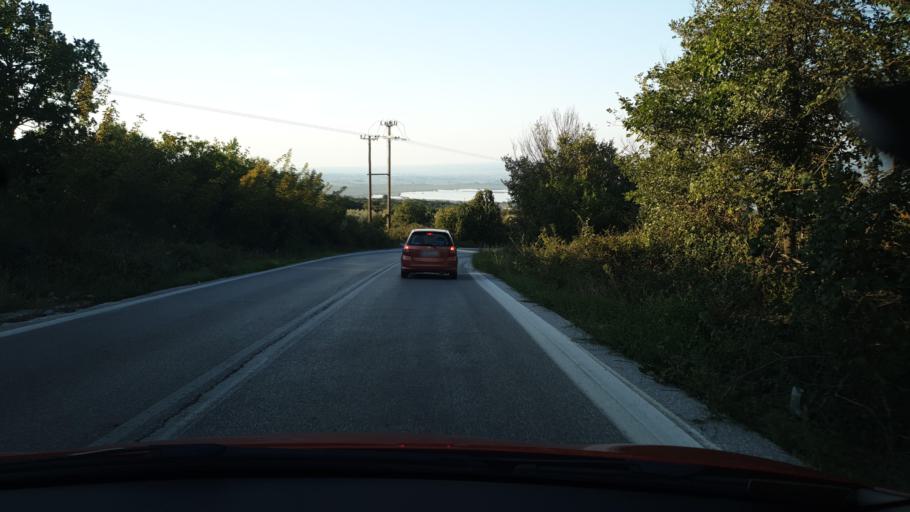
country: GR
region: Central Macedonia
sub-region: Nomos Thessalonikis
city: Agios Vasileios
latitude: 40.6462
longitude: 23.1133
